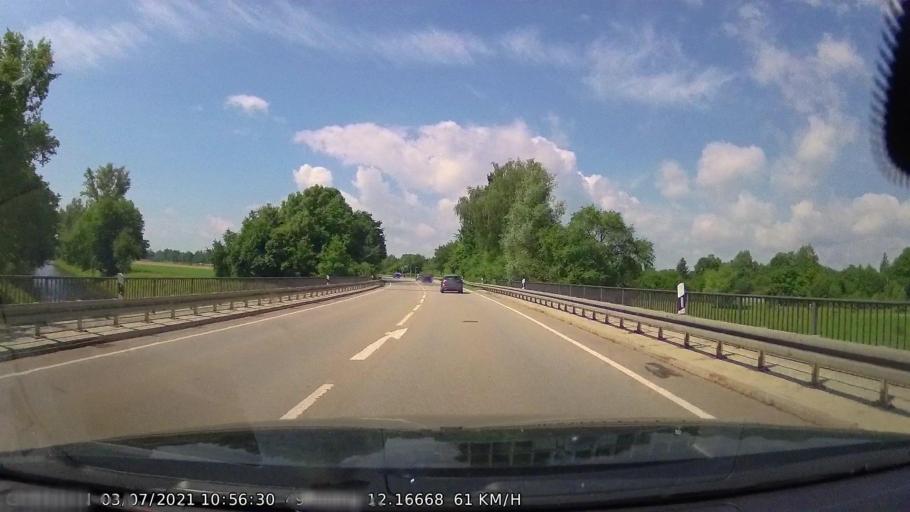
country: DE
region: Bavaria
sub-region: Upper Palatinate
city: Weiden
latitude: 49.6682
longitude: 12.1667
